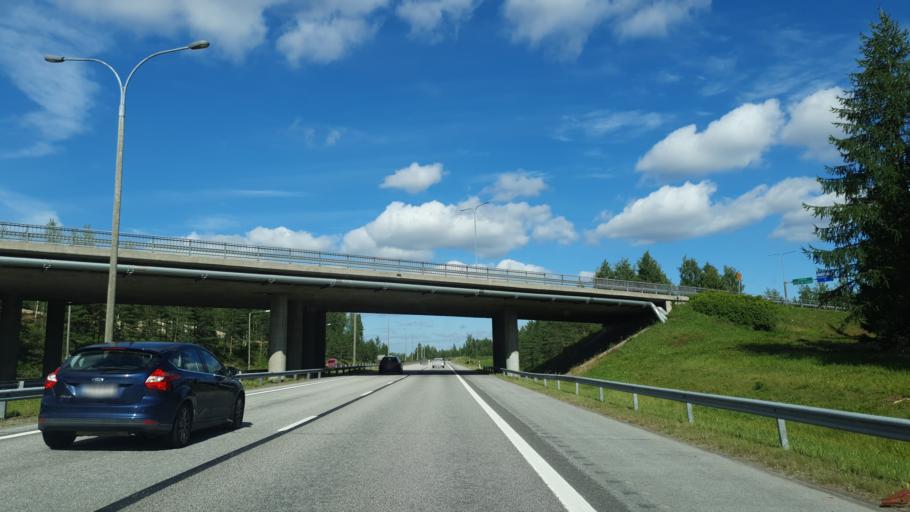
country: FI
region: Central Finland
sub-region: Jyvaeskylae
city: Jyvaeskylae
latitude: 62.1898
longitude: 25.6977
